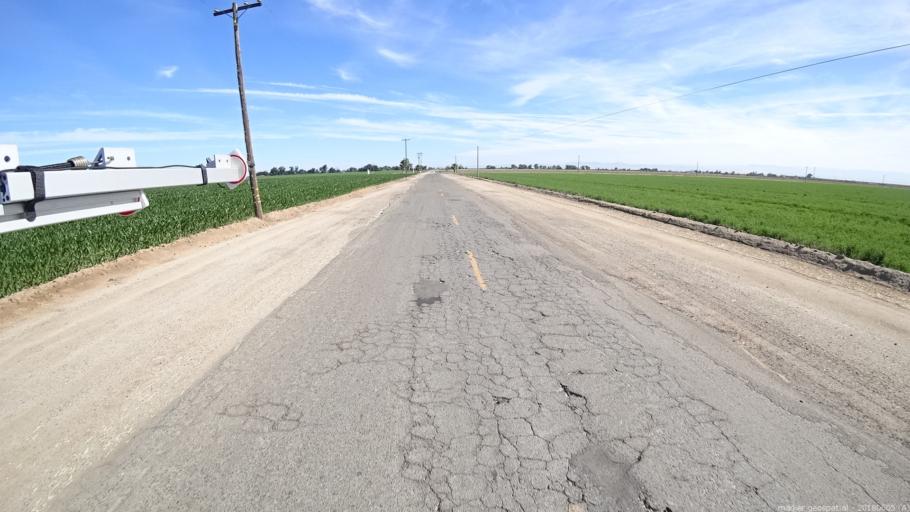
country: US
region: California
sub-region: Madera County
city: Chowchilla
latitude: 37.1400
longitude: -120.2927
